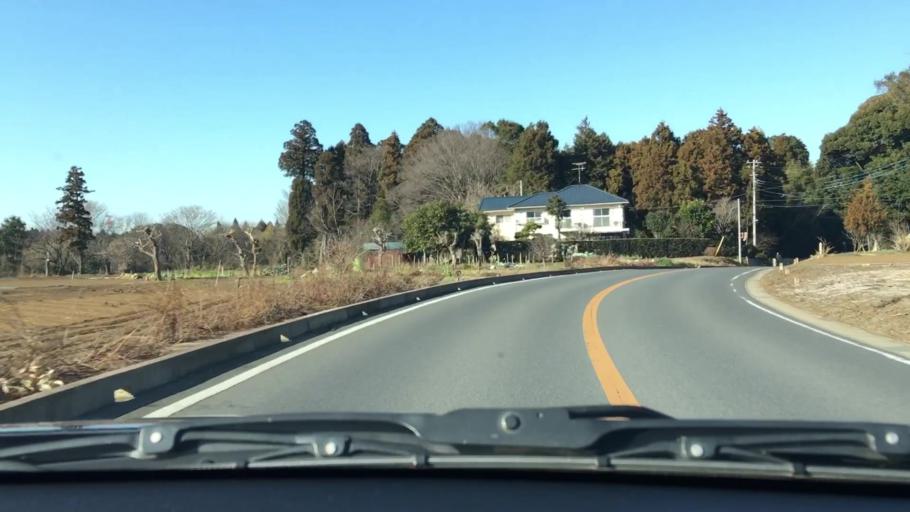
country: JP
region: Chiba
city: Shisui
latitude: 35.6981
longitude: 140.2536
